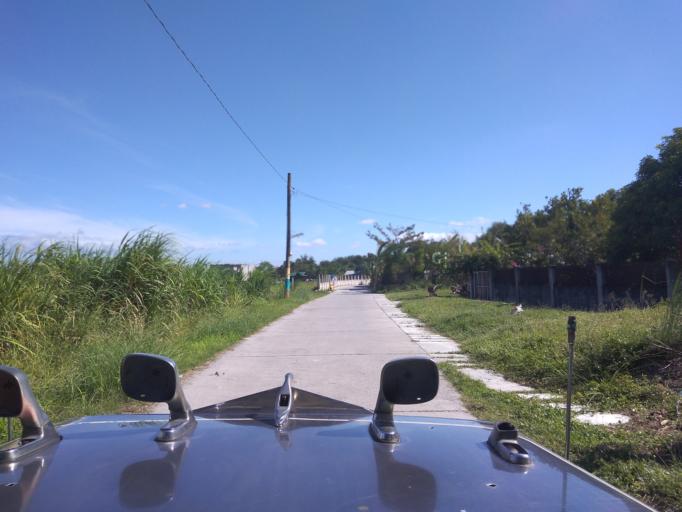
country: PH
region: Central Luzon
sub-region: Province of Pampanga
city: Magliman
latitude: 15.0265
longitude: 120.6334
